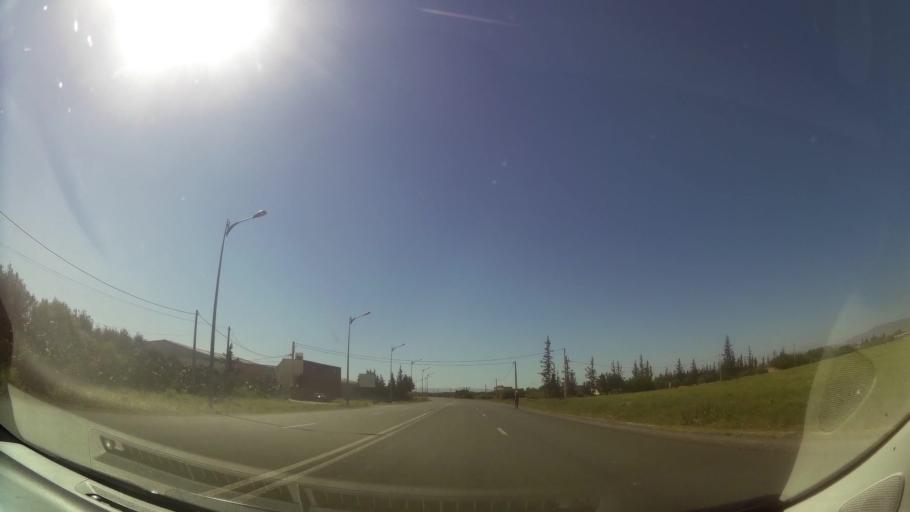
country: MA
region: Oriental
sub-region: Oujda-Angad
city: Oujda
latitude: 34.7338
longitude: -1.8759
